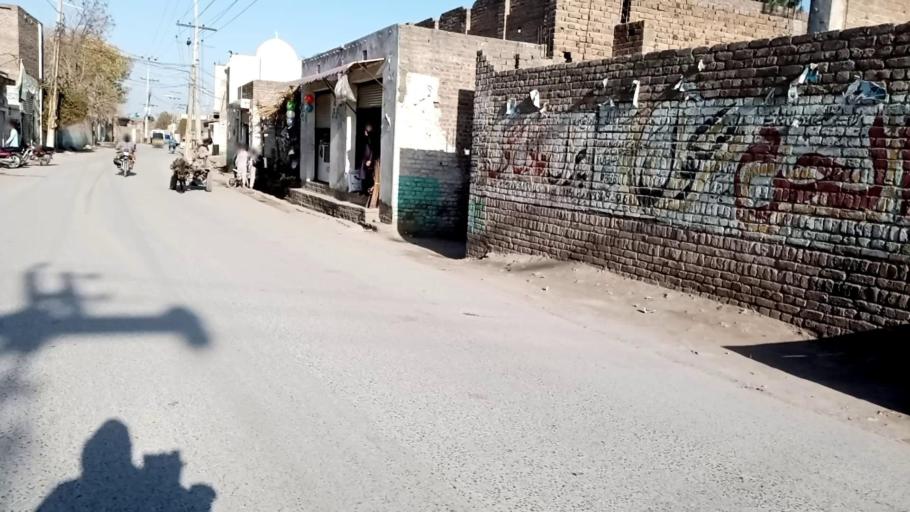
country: PK
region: Khyber Pakhtunkhwa
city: Peshawar
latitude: 34.0542
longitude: 71.5331
